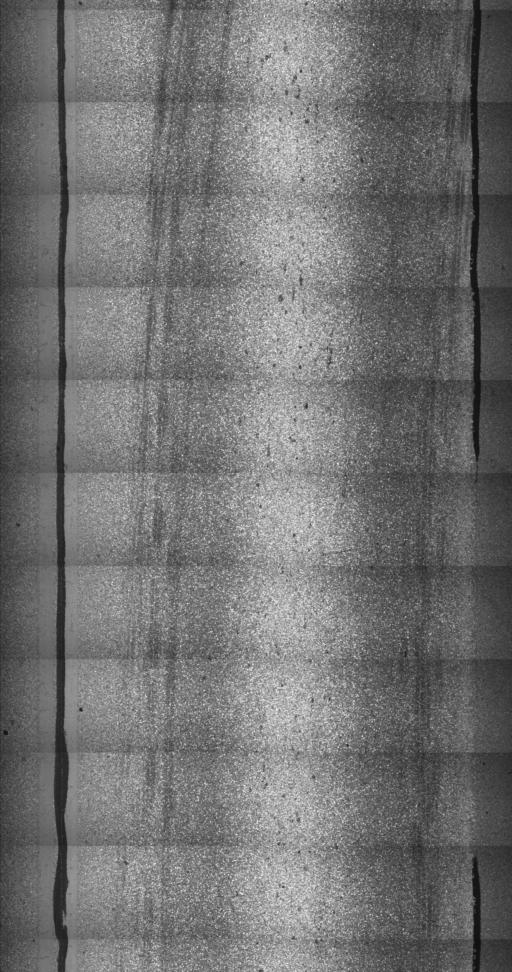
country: US
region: Vermont
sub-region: Chittenden County
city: Milton
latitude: 44.6742
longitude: -73.0191
